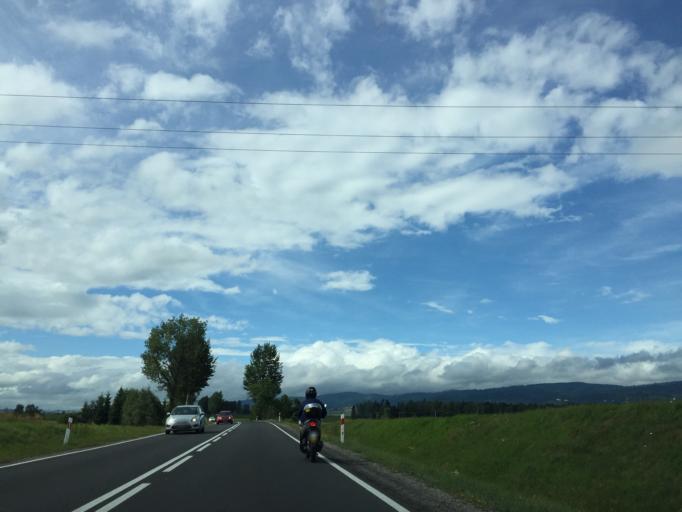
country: PL
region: Lesser Poland Voivodeship
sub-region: Powiat nowotarski
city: Waksmund
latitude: 49.4484
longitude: 20.0771
